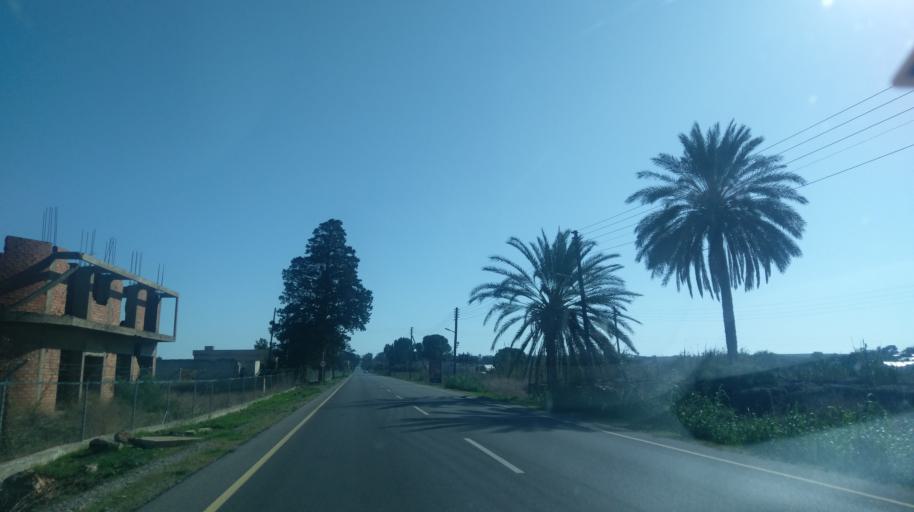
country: CY
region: Ammochostos
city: Deryneia
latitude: 35.0883
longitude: 33.9543
